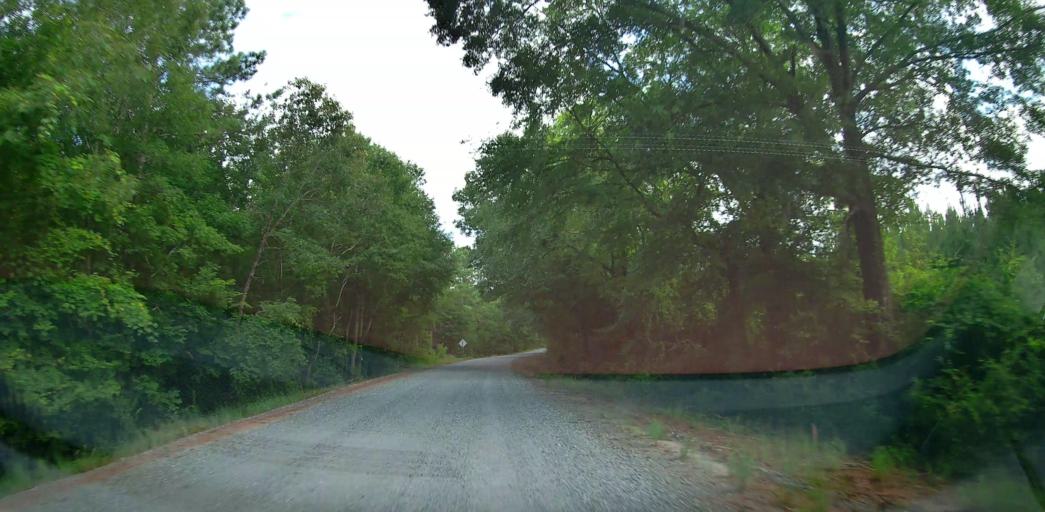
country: US
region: Georgia
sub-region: Bleckley County
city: Cochran
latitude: 32.4205
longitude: -83.4528
